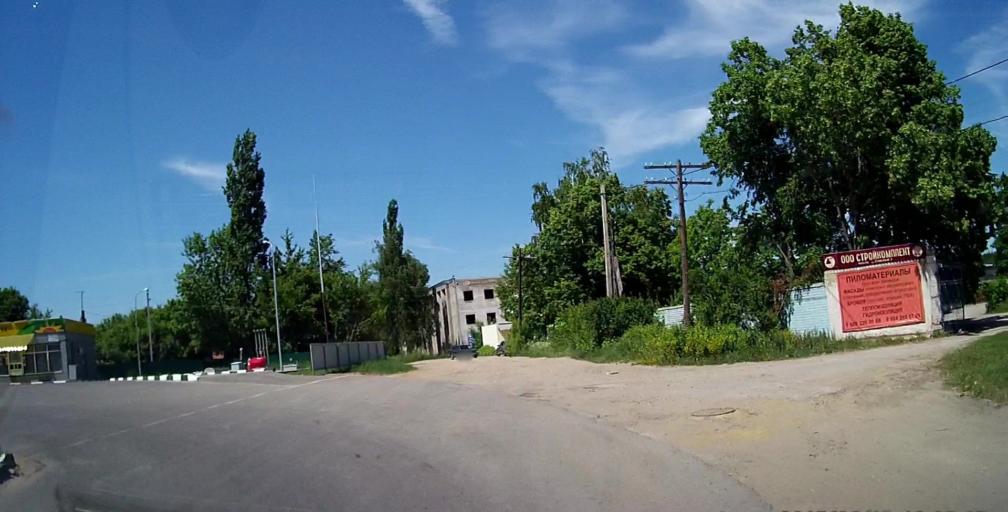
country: RU
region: Lipetsk
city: Chaplygin
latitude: 53.2491
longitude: 39.9735
